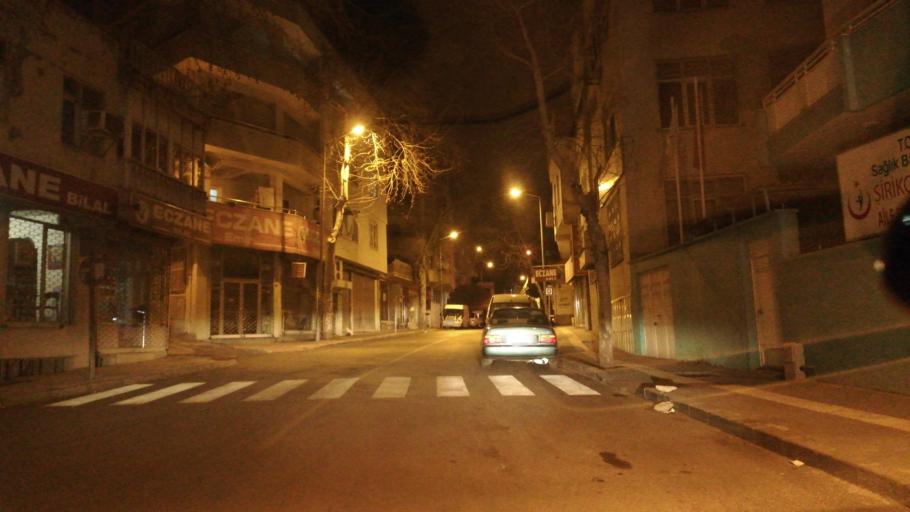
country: TR
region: Kahramanmaras
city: Kahramanmaras
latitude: 37.5916
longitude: 36.9307
